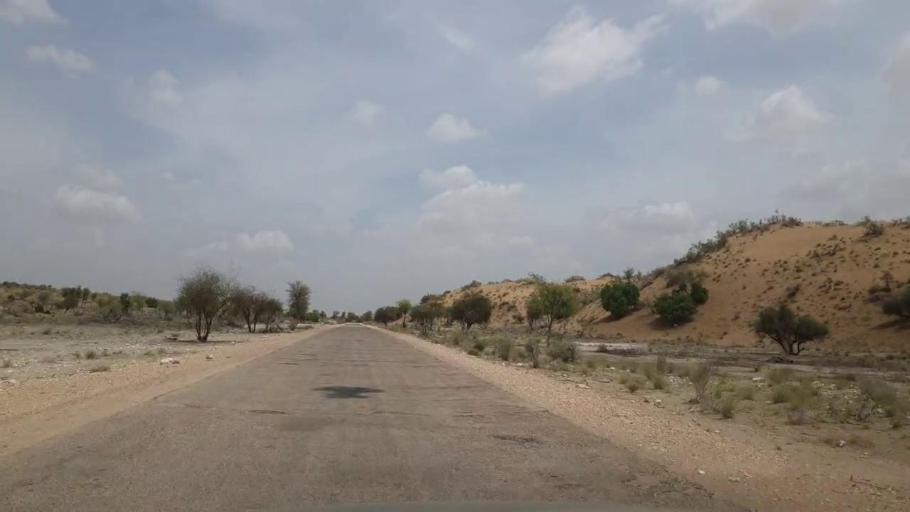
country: PK
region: Sindh
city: Kot Diji
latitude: 27.1697
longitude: 69.2125
